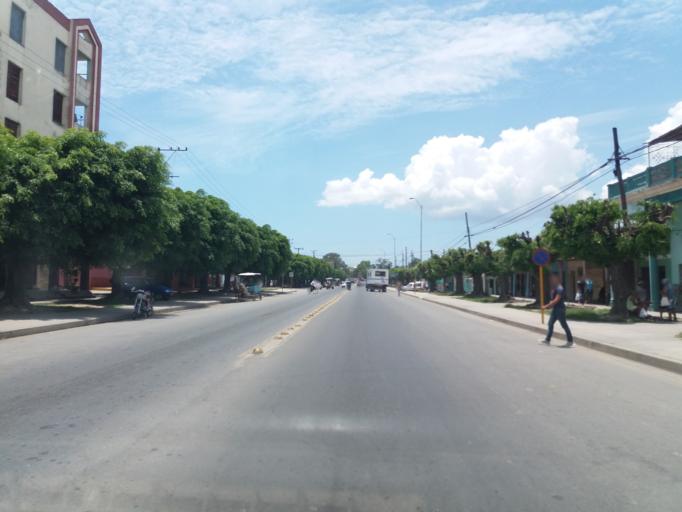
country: CU
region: Cienfuegos
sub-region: Municipio de Cienfuegos
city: Cienfuegos
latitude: 22.1508
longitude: -80.4416
